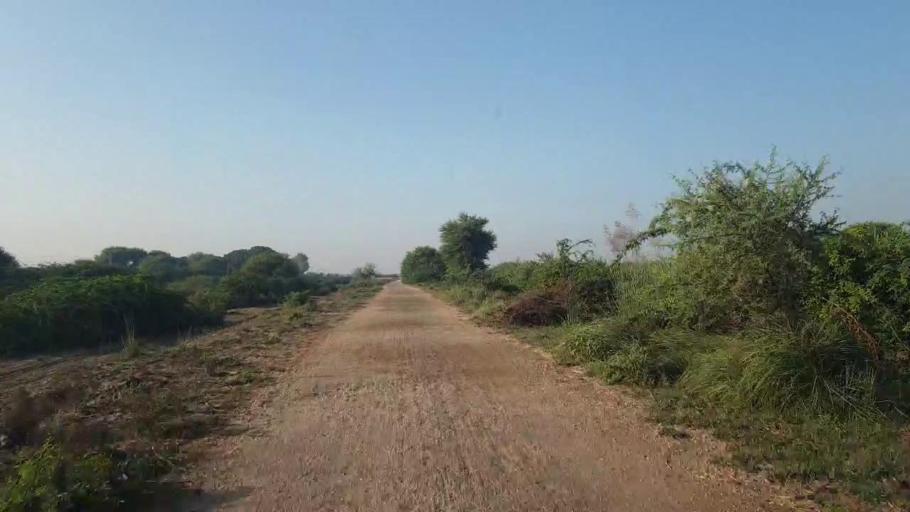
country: PK
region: Sindh
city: Badin
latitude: 24.5969
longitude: 68.7733
